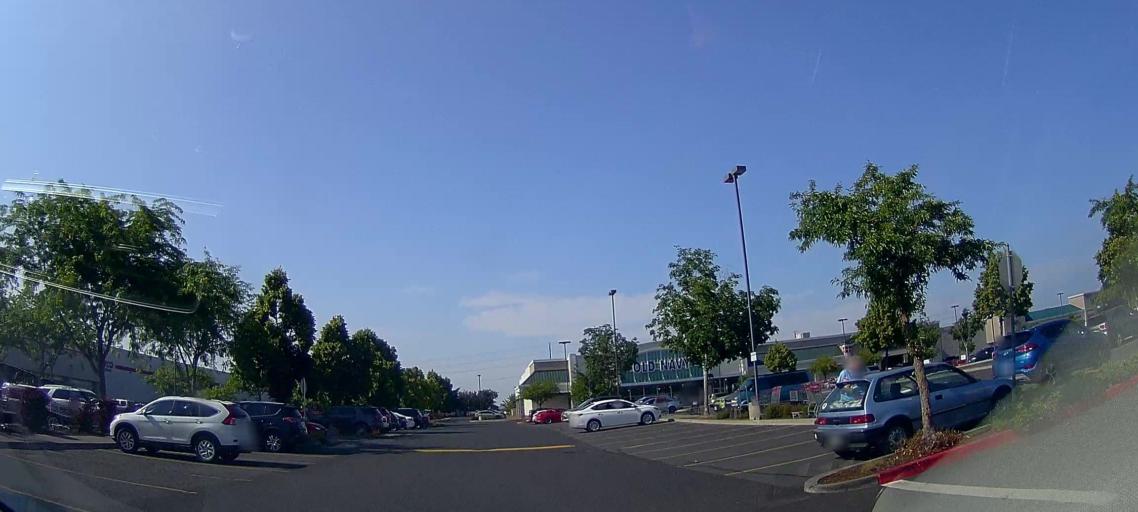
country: US
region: Oregon
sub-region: Deschutes County
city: Bend
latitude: 44.0563
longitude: -121.2664
